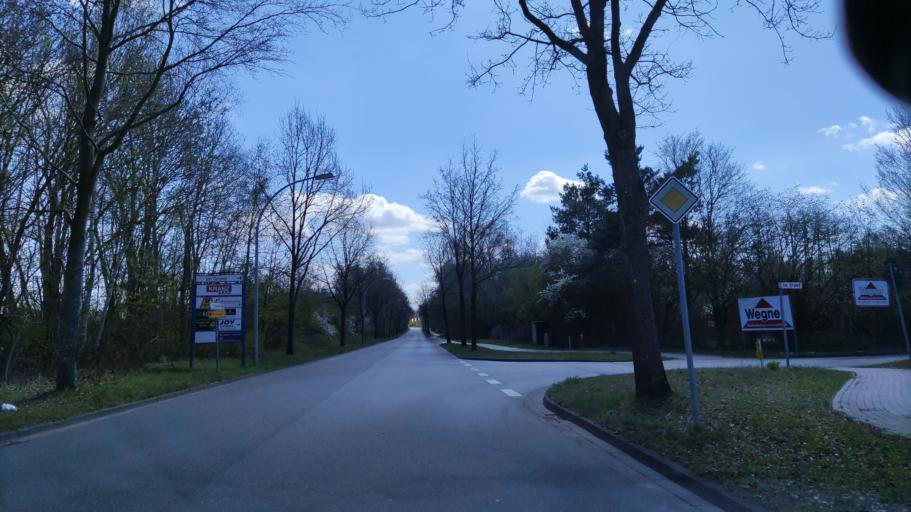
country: DE
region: Lower Saxony
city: Uelzen
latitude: 52.9927
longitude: 10.5485
